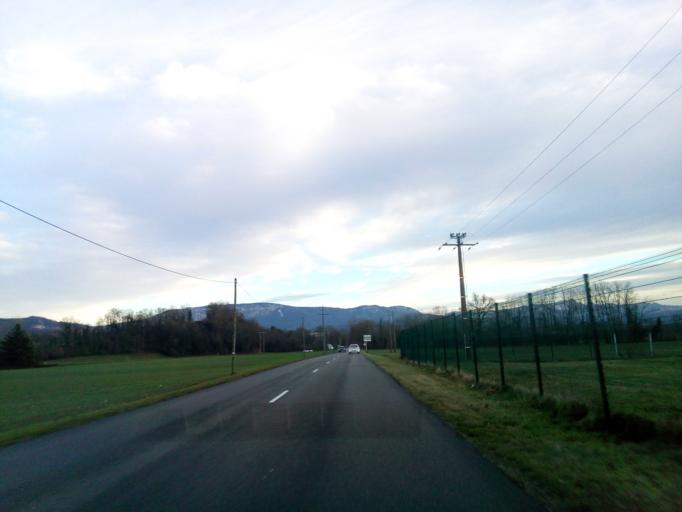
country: FR
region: Rhone-Alpes
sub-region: Departement de l'Isere
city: Romagnieu
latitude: 45.5673
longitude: 5.6642
